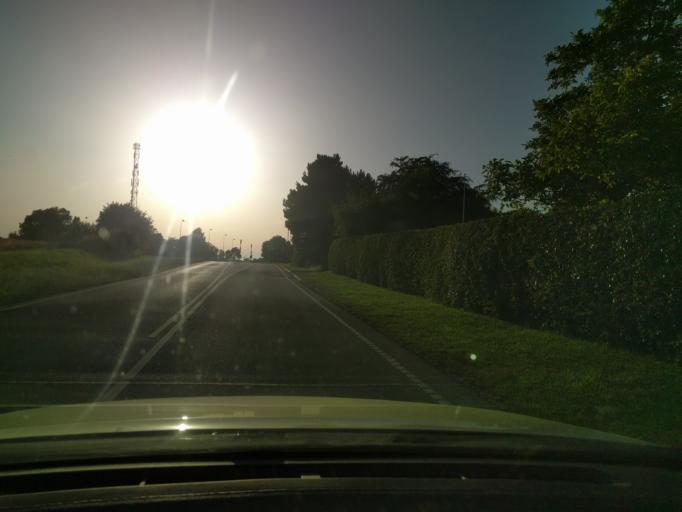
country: DK
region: Zealand
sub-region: Vordingborg Kommune
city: Stege
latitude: 55.0056
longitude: 12.1461
